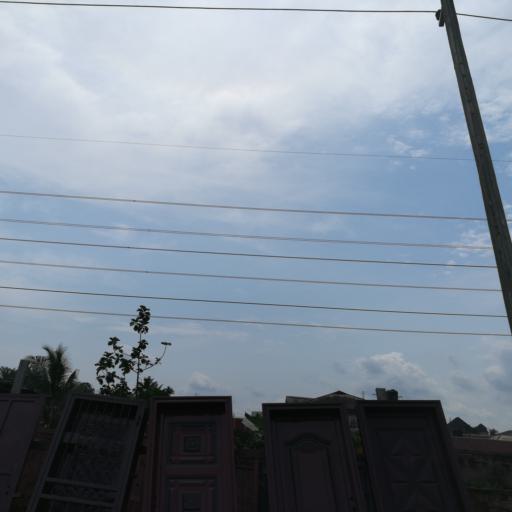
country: NG
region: Rivers
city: Port Harcourt
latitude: 4.8647
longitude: 7.0191
